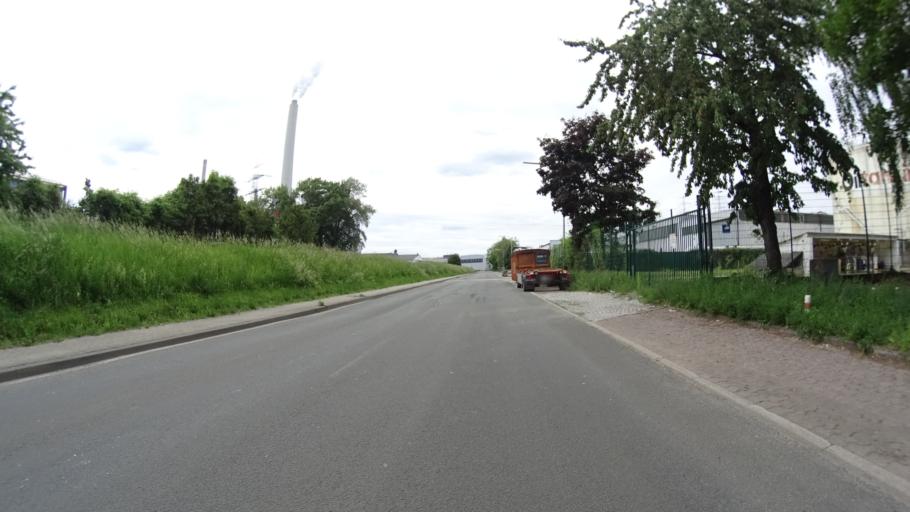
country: DE
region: Baden-Wuerttemberg
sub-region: Karlsruhe Region
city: Rheinstetten
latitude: 49.0124
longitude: 8.3156
